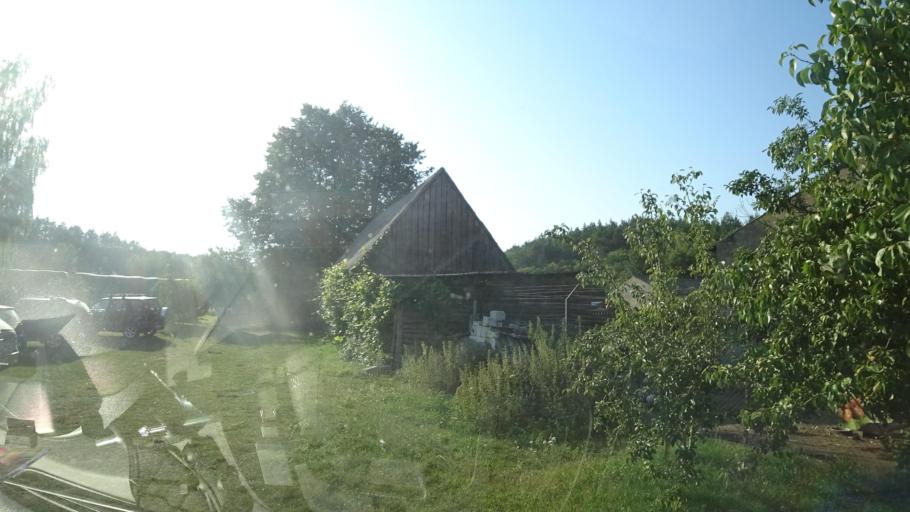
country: PL
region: Pomeranian Voivodeship
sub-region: Powiat chojnicki
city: Brusy
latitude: 53.8695
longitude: 17.5471
